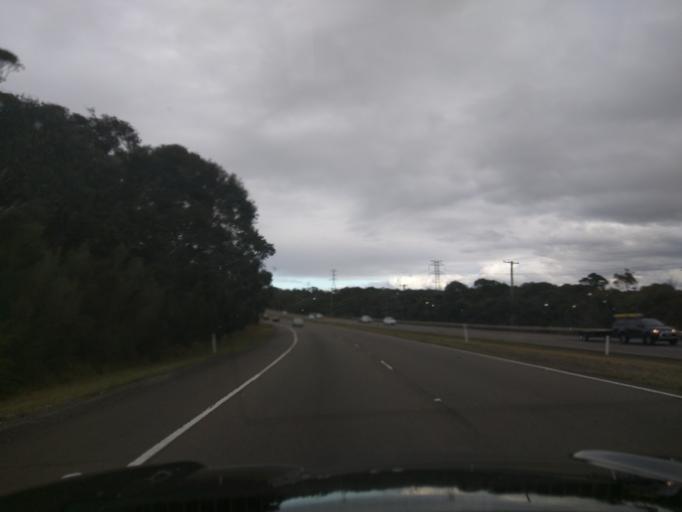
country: AU
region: New South Wales
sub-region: Sutherland Shire
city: Heathcote
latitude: -34.1138
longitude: 150.9921
